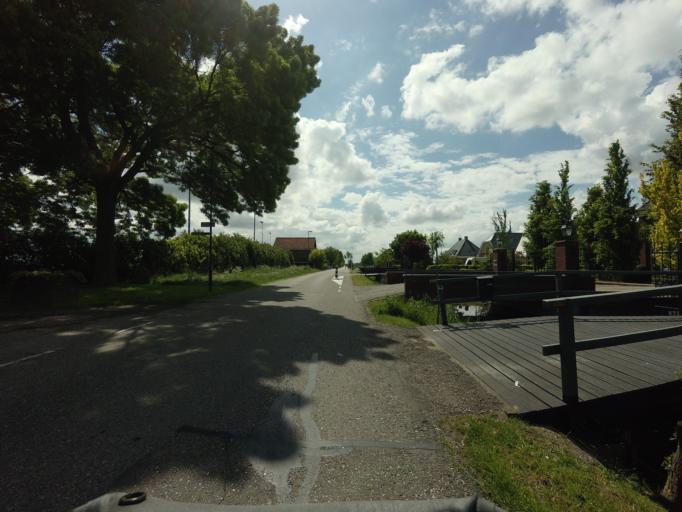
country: NL
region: South Holland
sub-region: Gemeente Gorinchem
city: Gorinchem
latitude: 51.8726
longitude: 4.9482
